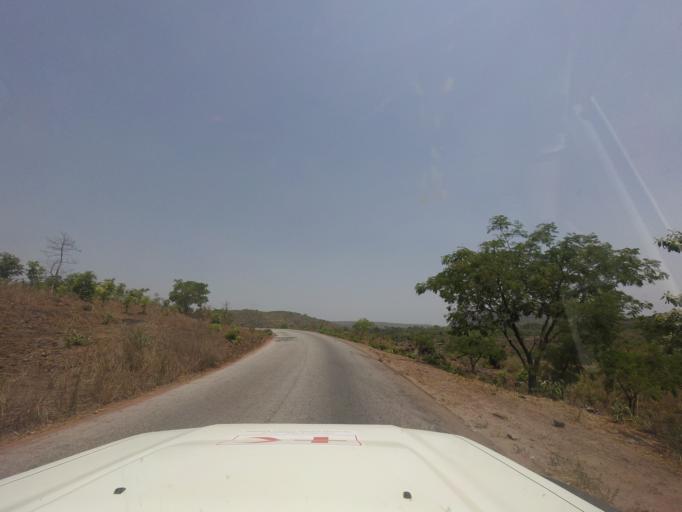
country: GN
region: Kindia
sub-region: Coyah
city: Coyah
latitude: 9.8318
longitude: -13.1206
